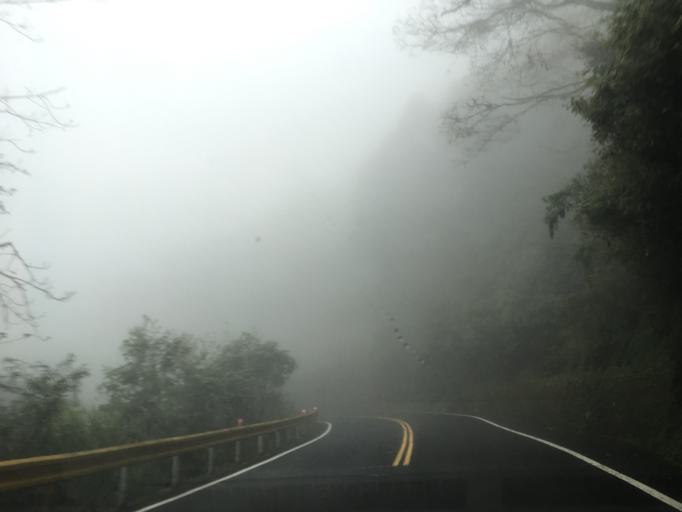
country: TW
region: Taiwan
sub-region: Hualien
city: Hualian
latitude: 24.1947
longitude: 121.4229
